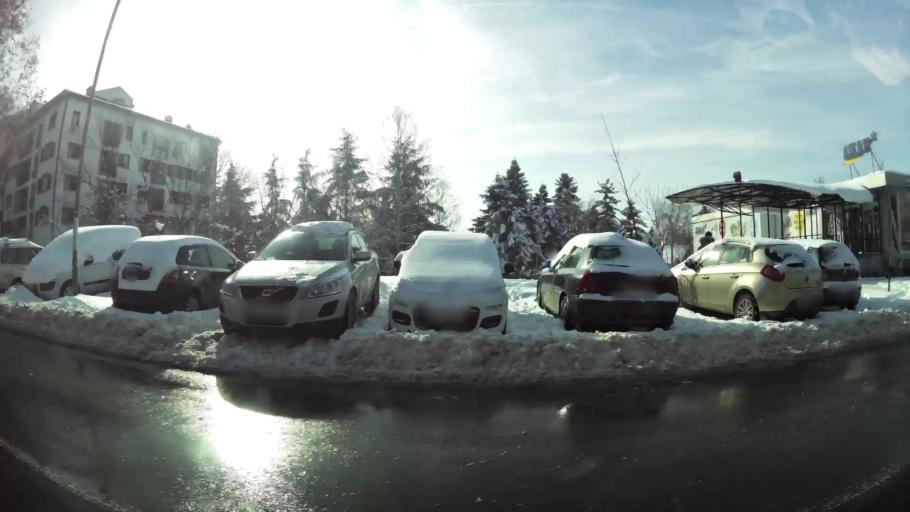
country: RS
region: Central Serbia
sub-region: Belgrade
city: Zvezdara
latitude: 44.7933
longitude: 20.5373
